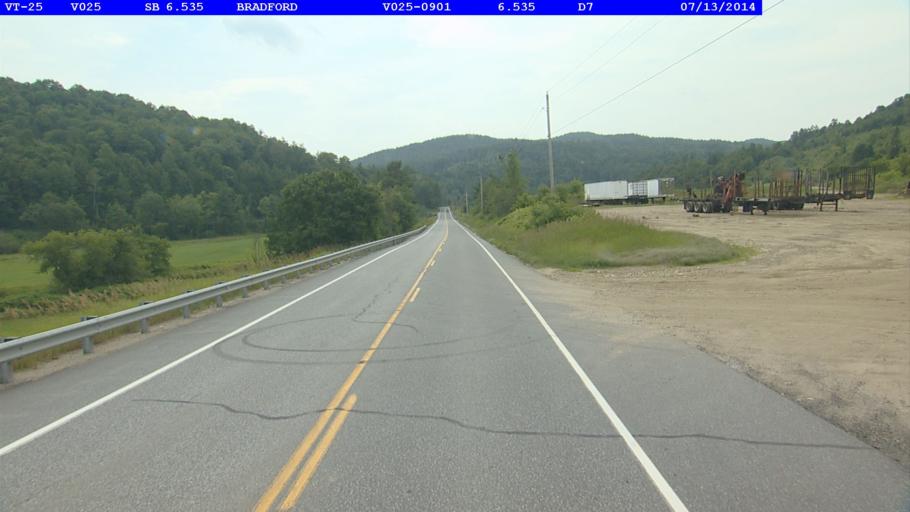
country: US
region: New Hampshire
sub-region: Grafton County
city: Haverhill
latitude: 44.0364
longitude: -72.1973
